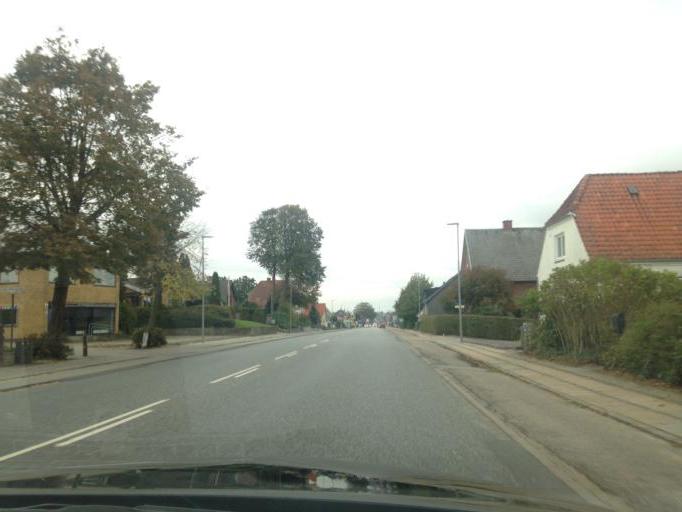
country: DK
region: South Denmark
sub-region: Kolding Kommune
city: Kolding
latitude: 55.4725
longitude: 9.4707
